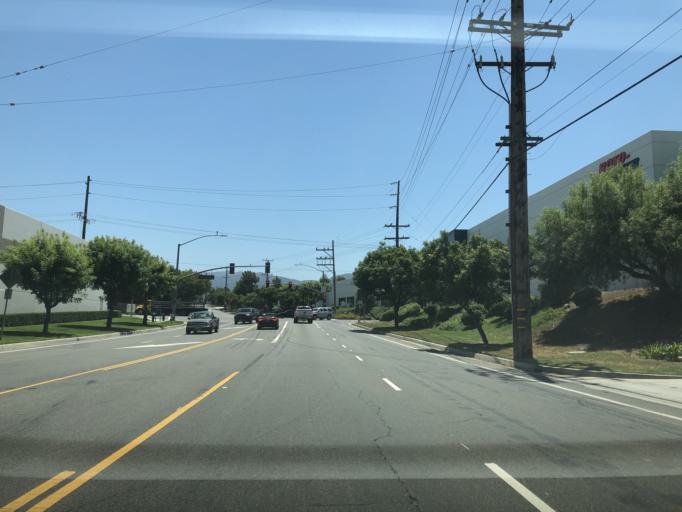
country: US
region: California
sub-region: Riverside County
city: Corona
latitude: 33.8921
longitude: -117.5920
